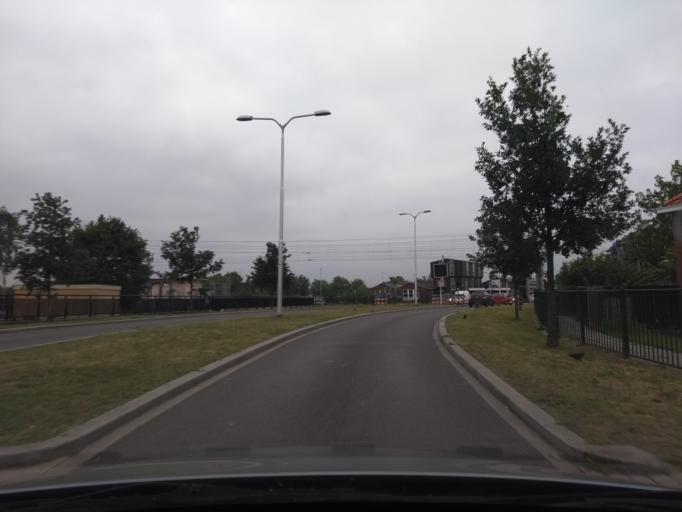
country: NL
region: Overijssel
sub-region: Gemeente Almelo
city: Almelo
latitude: 52.3620
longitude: 6.6455
